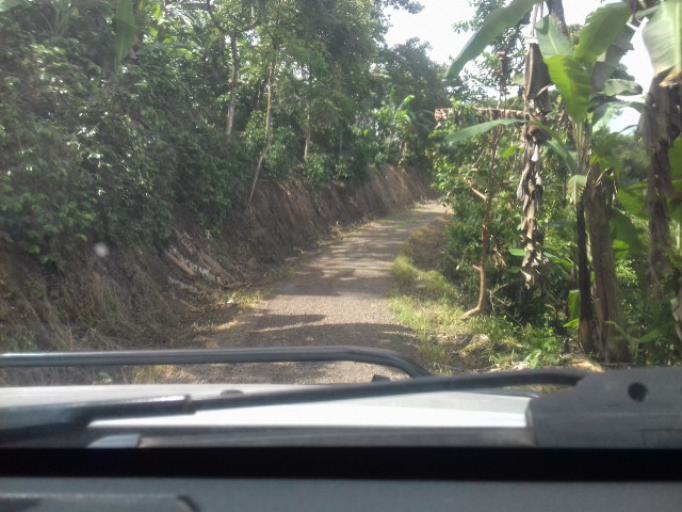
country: NI
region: Atlantico Norte (RAAN)
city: Waslala
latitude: 13.2151
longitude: -85.5758
